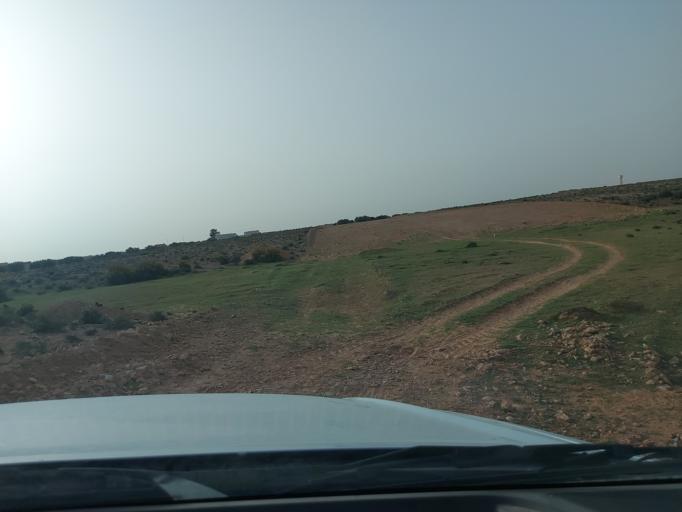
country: TN
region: Madanin
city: Medenine
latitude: 33.3387
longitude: 10.5943
